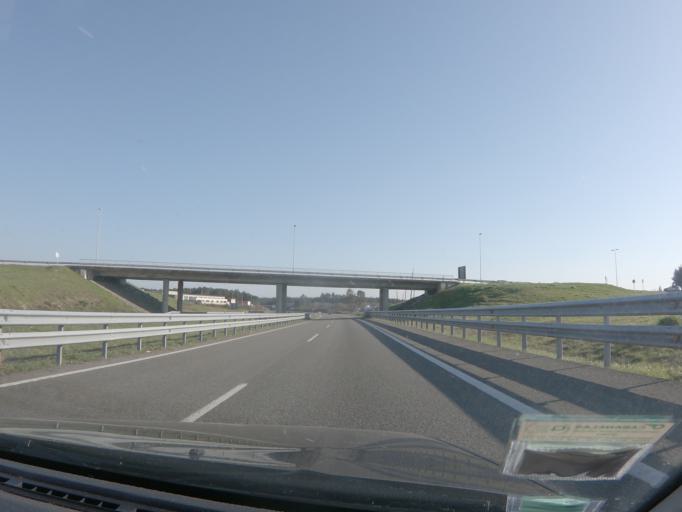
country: ES
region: Galicia
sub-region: Provincia de Lugo
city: Outeiro de Rei
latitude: 43.1073
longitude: -7.6038
